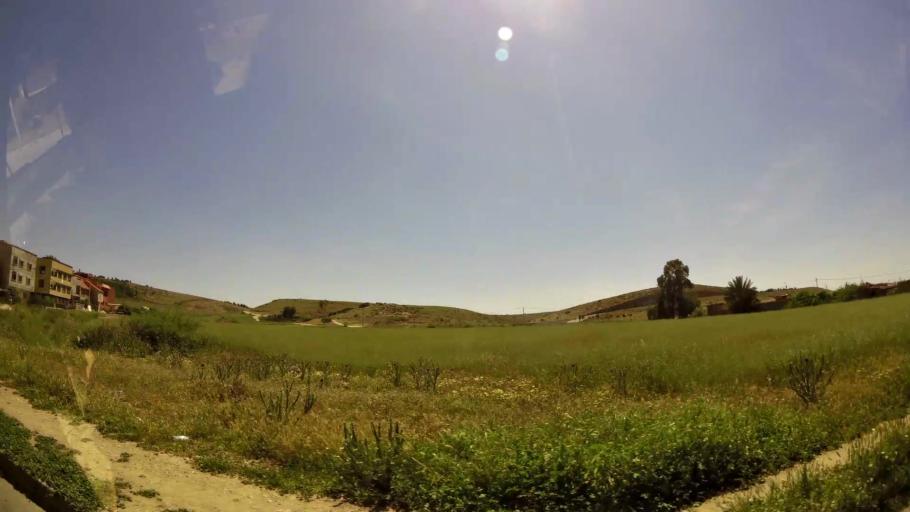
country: MA
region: Oriental
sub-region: Oujda-Angad
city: Oujda
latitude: 34.6502
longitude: -1.9126
